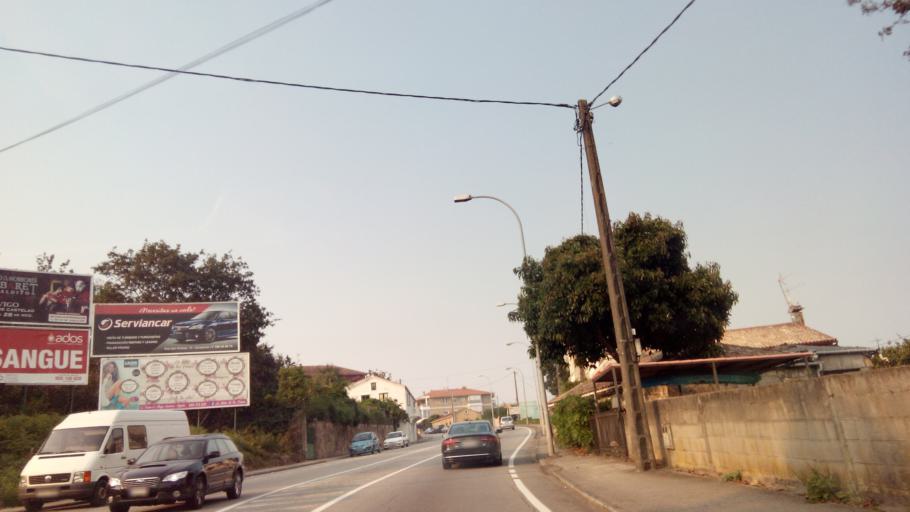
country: ES
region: Galicia
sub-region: Provincia de Pontevedra
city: Nigran
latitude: 42.1204
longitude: -8.8121
